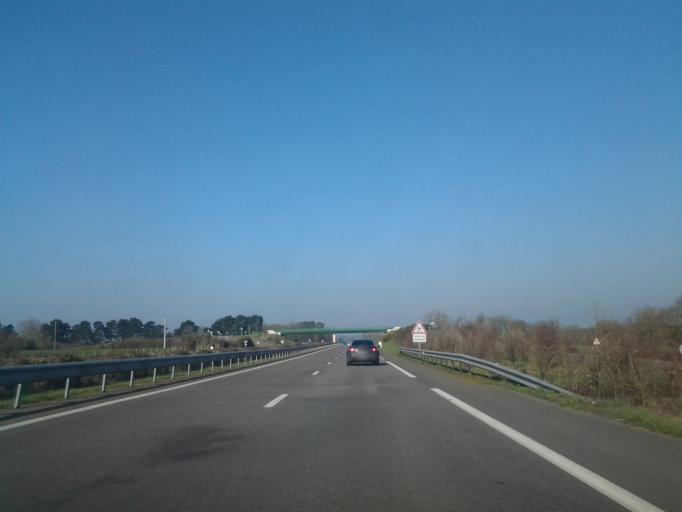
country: FR
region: Pays de la Loire
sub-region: Departement de la Vendee
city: Saint-Christophe-du-Ligneron
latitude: 46.8011
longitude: -1.7268
